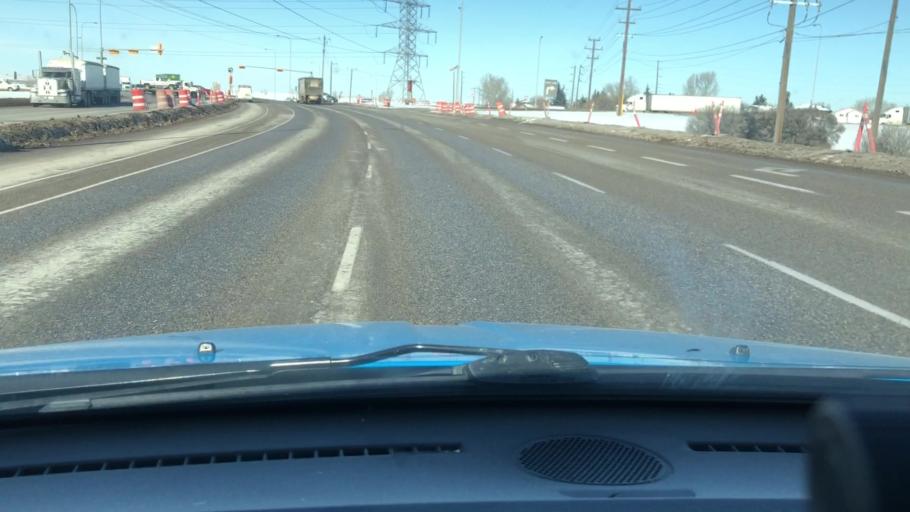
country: CA
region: Alberta
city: Calgary
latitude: 51.0138
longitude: -114.0018
